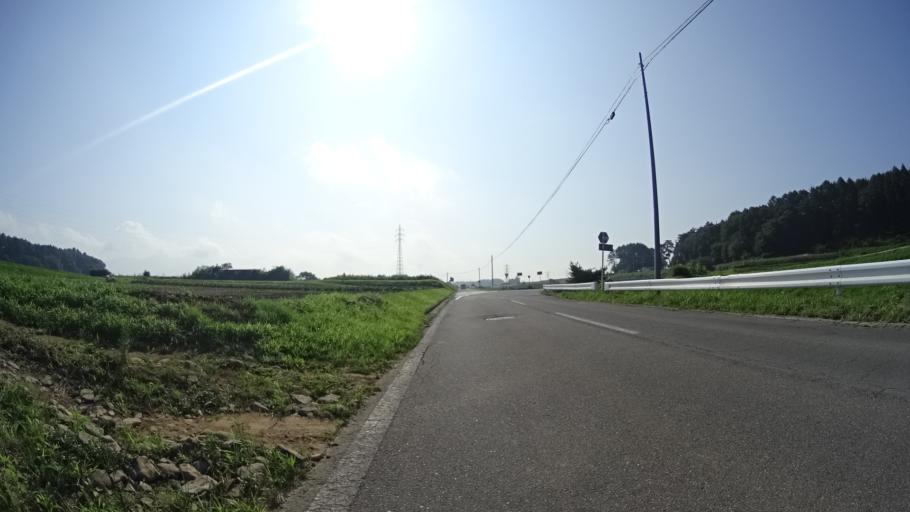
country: JP
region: Nagano
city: Chino
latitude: 35.9689
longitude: 138.1878
